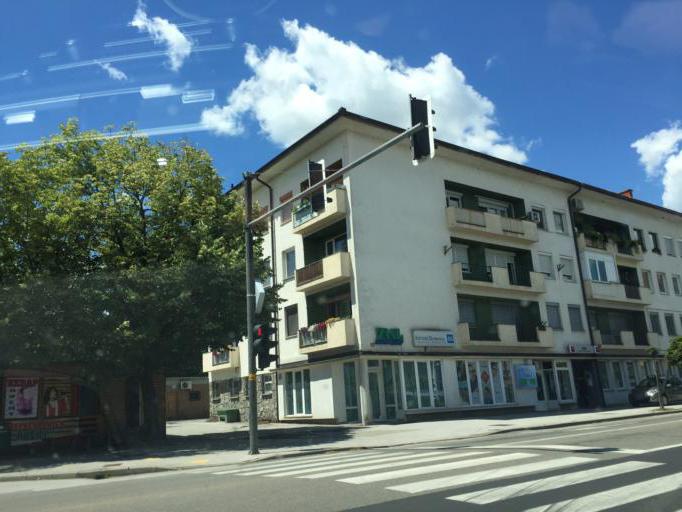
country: SI
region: Gornja Radgona
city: Gornja Radgona
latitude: 46.6768
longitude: 15.9911
